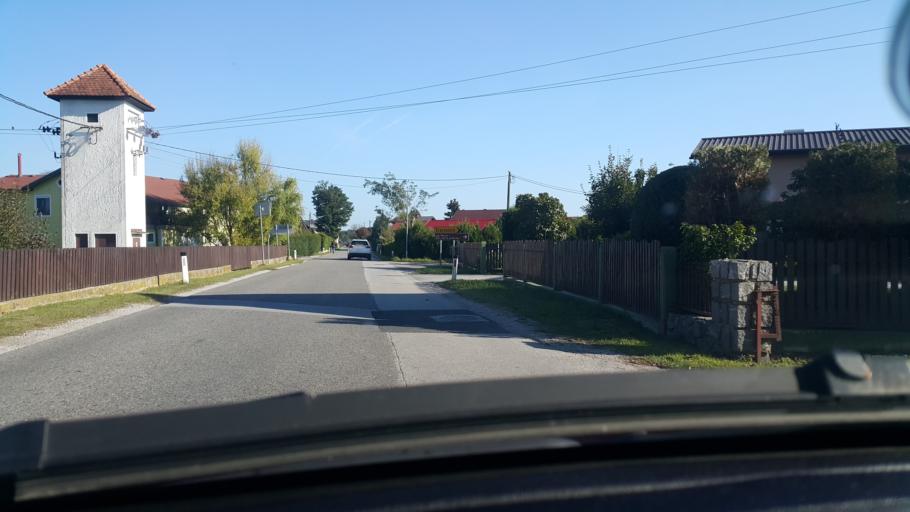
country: SI
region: Race-Fram
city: Race
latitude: 46.4399
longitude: 15.7244
